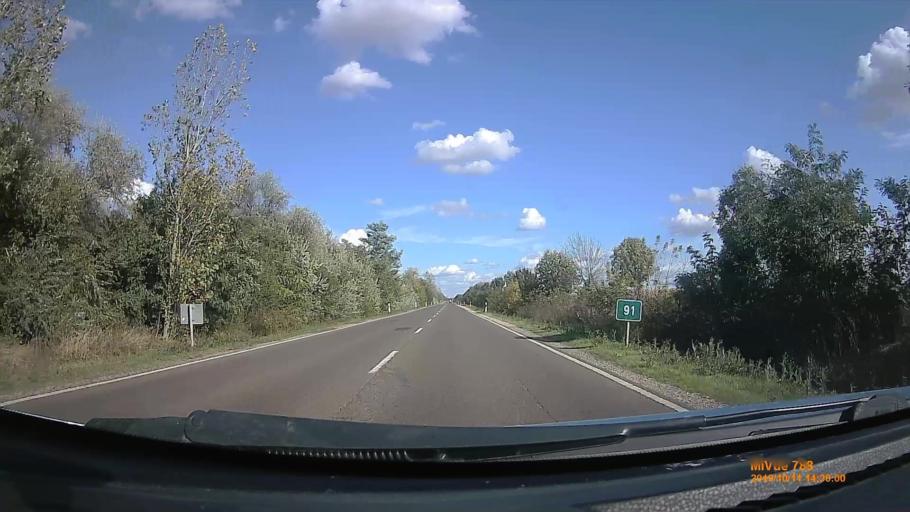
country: HU
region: Hajdu-Bihar
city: Balmazujvaros
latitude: 47.5597
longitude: 21.3926
